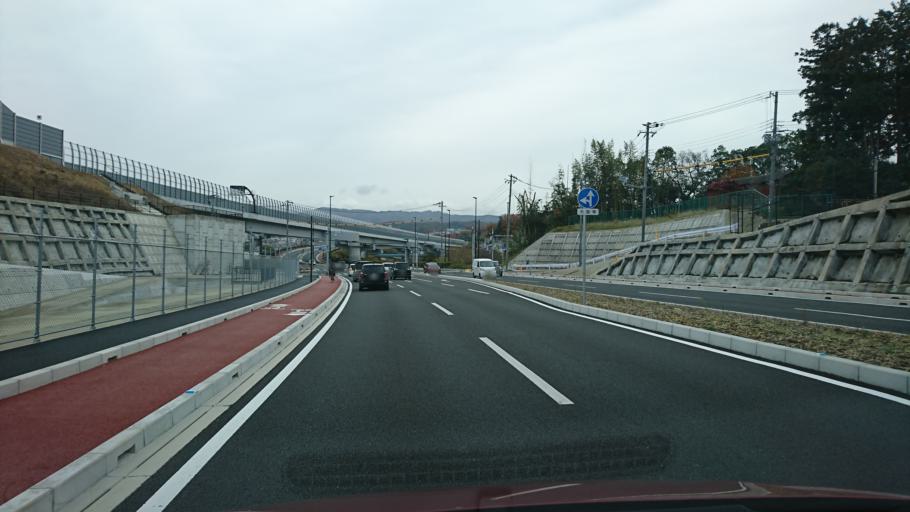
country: JP
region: Osaka
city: Ikeda
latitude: 34.8846
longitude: 135.3980
